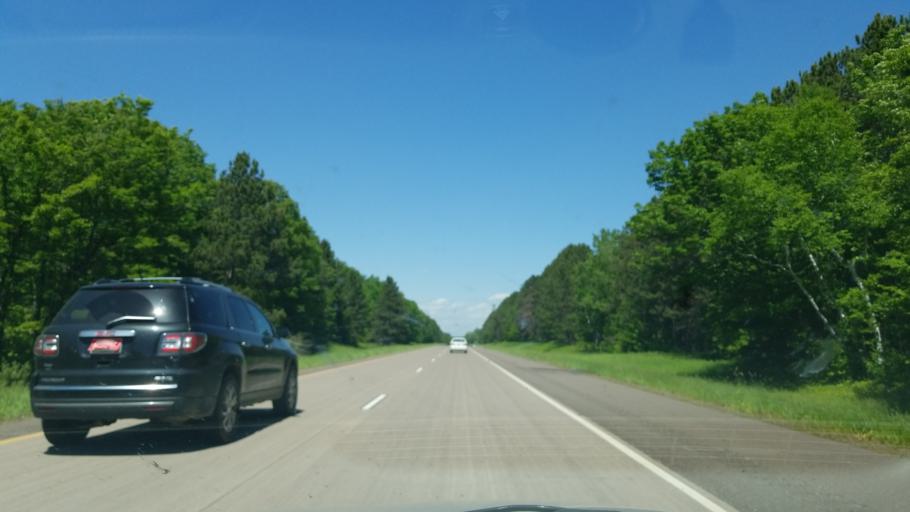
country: US
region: Minnesota
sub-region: Pine County
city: Sandstone
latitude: 46.0797
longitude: -92.8992
